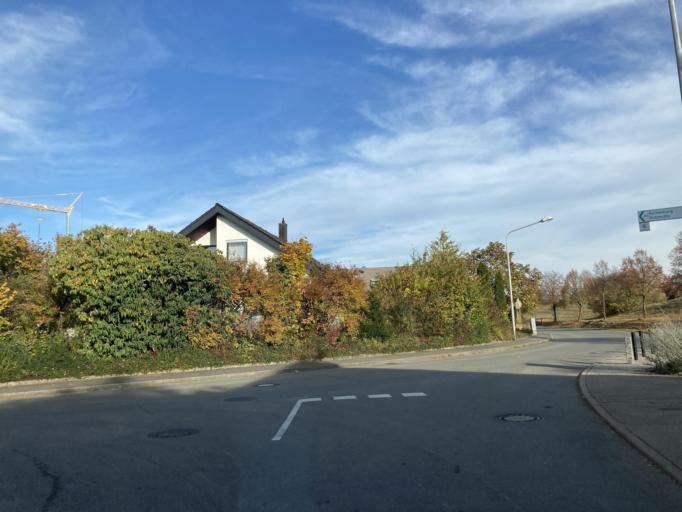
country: DE
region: Baden-Wuerttemberg
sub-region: Tuebingen Region
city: Bodelshausen
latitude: 48.3979
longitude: 8.9766
